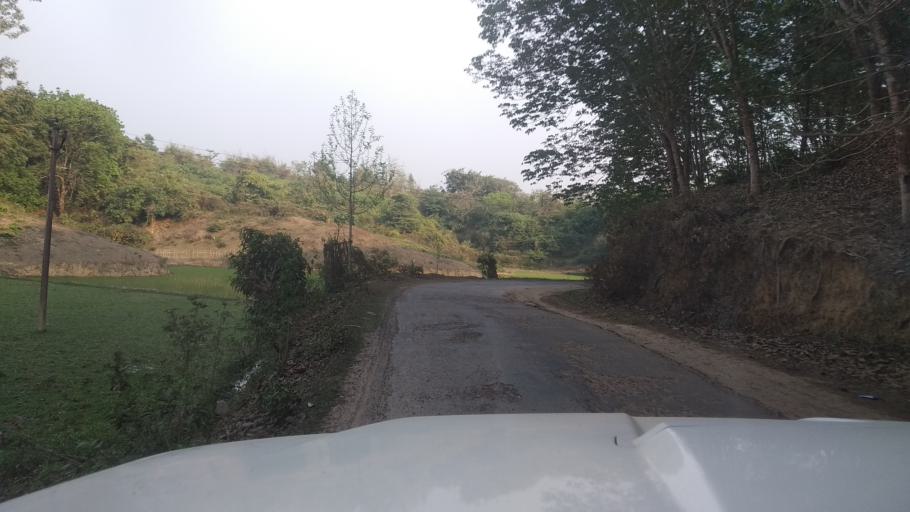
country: IN
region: Tripura
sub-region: West Tripura
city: Sonamura
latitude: 23.3445
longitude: 91.3205
